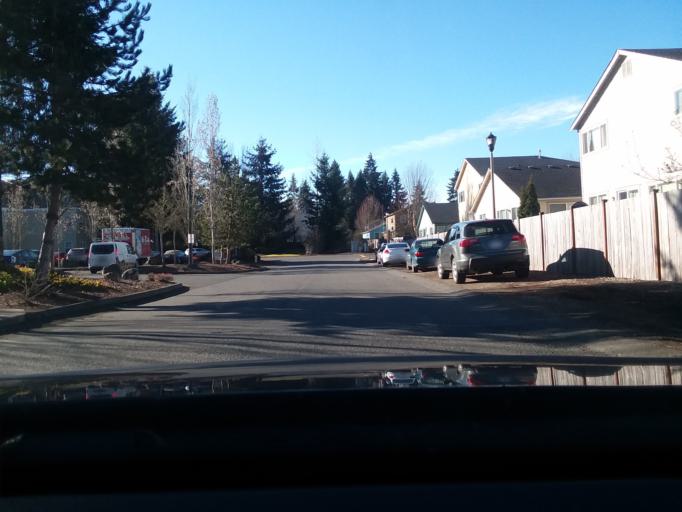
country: US
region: Washington
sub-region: Pierce County
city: Graham
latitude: 47.0961
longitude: -122.3086
